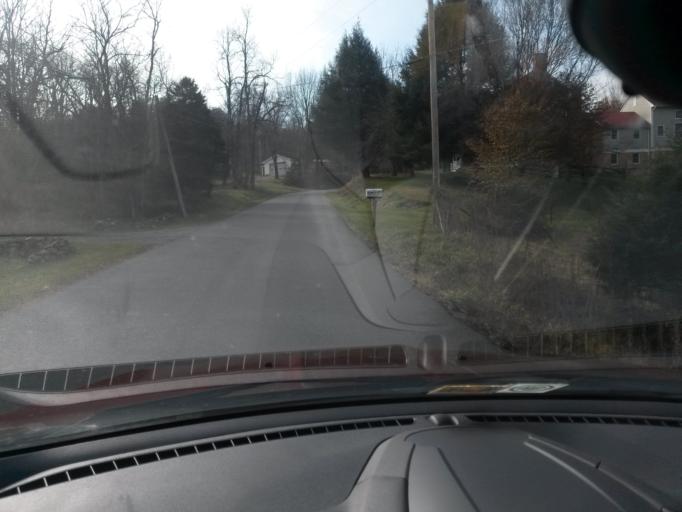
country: US
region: Virginia
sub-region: Botetourt County
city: Fincastle
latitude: 37.5914
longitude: -79.8641
